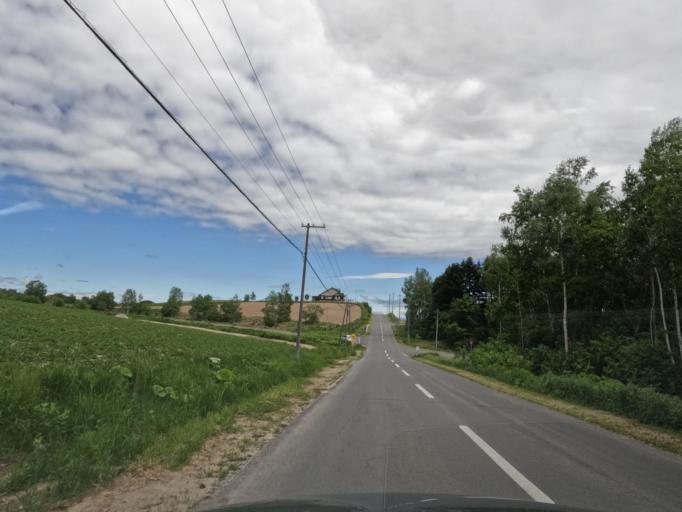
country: JP
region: Hokkaido
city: Shimo-furano
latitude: 43.5243
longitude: 142.4337
